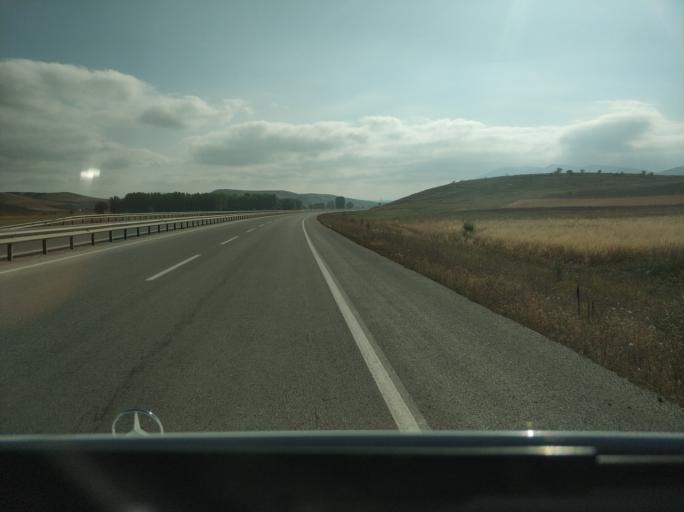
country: TR
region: Sivas
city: Yildizeli
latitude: 39.8502
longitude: 36.4972
